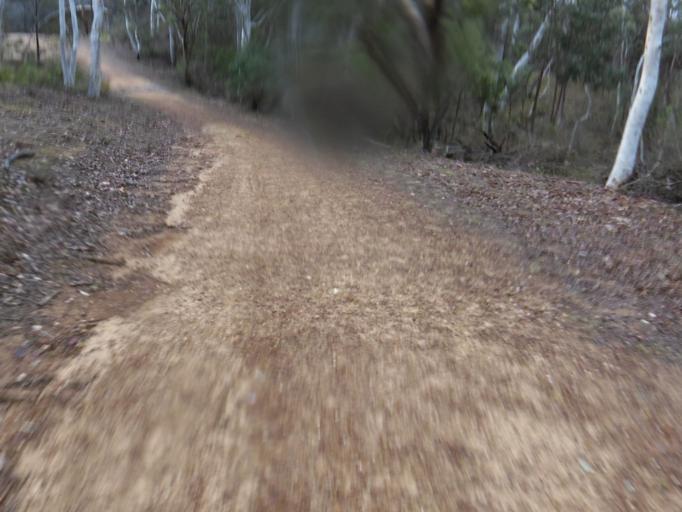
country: AU
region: Australian Capital Territory
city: Macquarie
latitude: -35.2679
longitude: 149.0878
